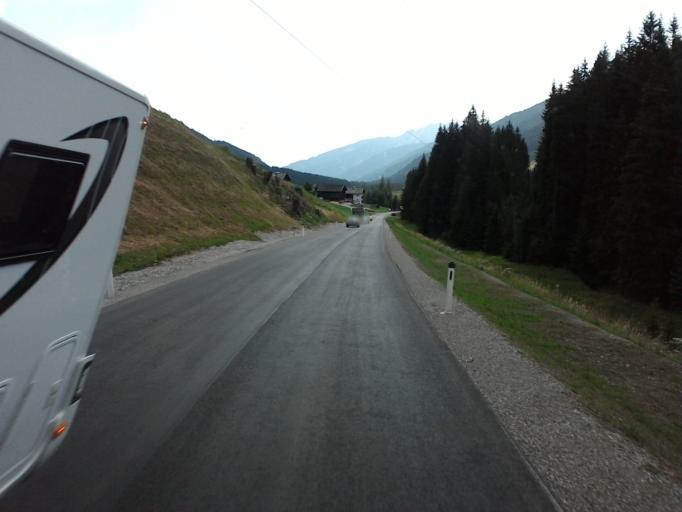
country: AT
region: Tyrol
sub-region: Politischer Bezirk Lienz
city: Abfaltersbach
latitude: 46.7157
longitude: 12.5573
